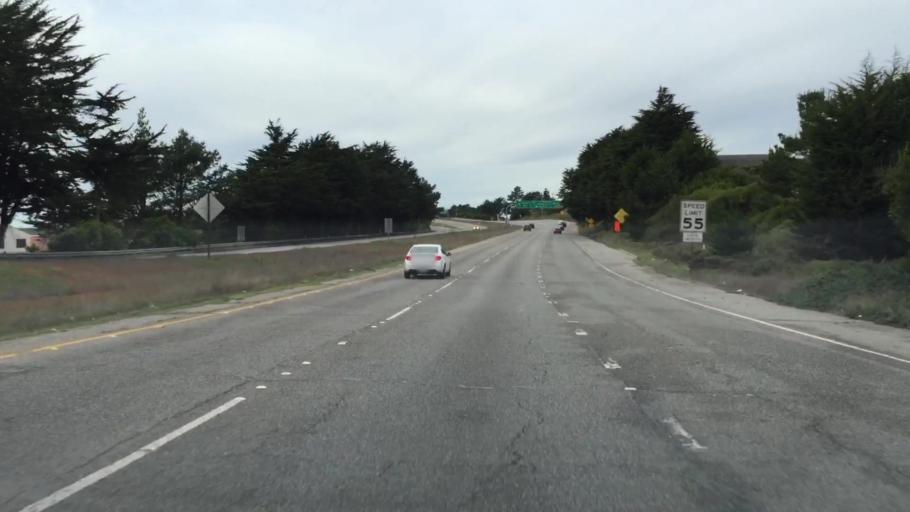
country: US
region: California
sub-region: San Mateo County
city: Broadmoor
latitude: 37.6639
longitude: -122.4788
